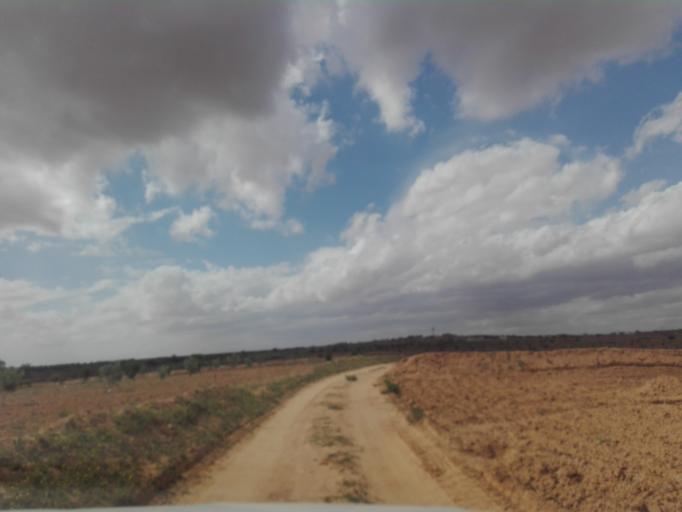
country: TN
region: Safaqis
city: Sfax
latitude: 34.6975
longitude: 10.4436
